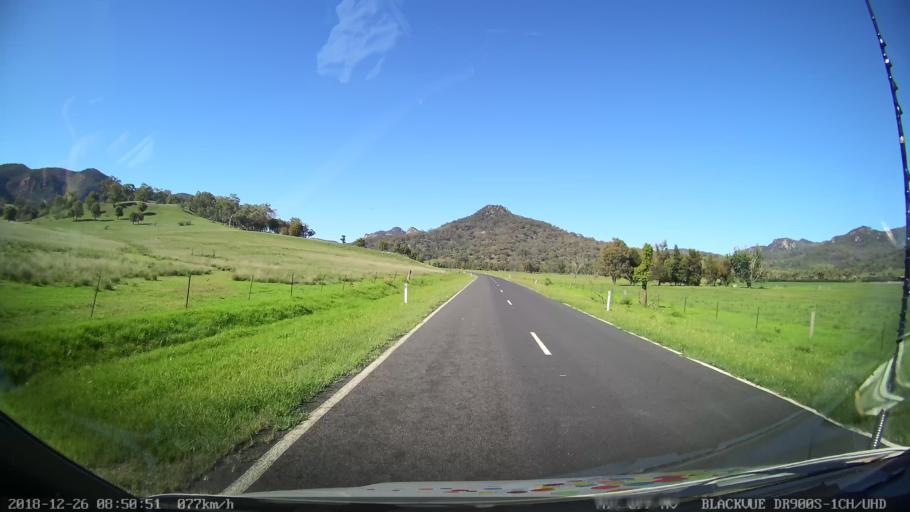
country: AU
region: New South Wales
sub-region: Mid-Western Regional
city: Kandos
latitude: -32.5801
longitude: 150.0922
